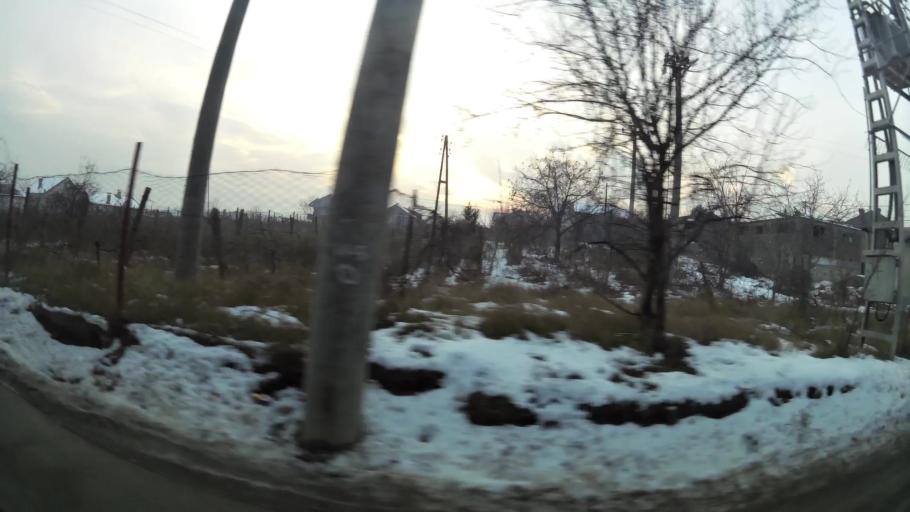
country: MK
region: Suto Orizari
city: Suto Orizare
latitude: 42.0317
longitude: 21.4169
